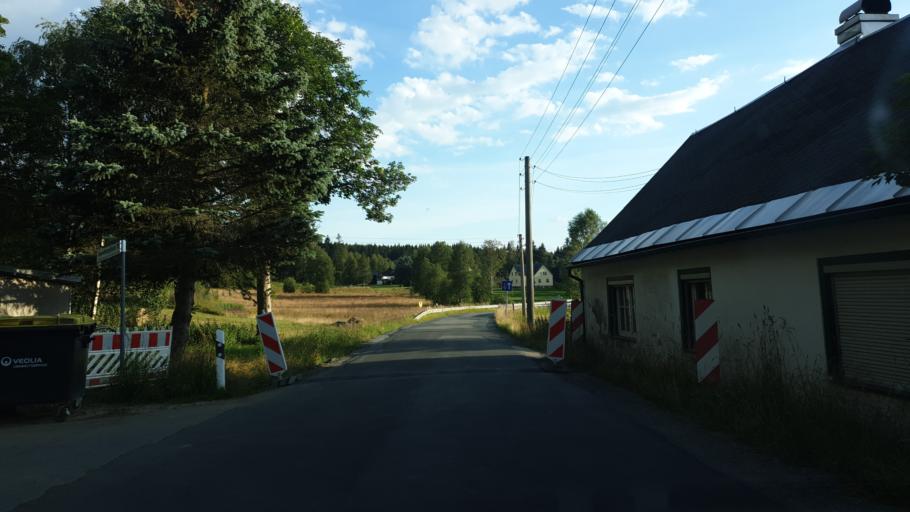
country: DE
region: Saxony
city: Hammerbrucke
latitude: 50.4353
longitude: 12.4309
